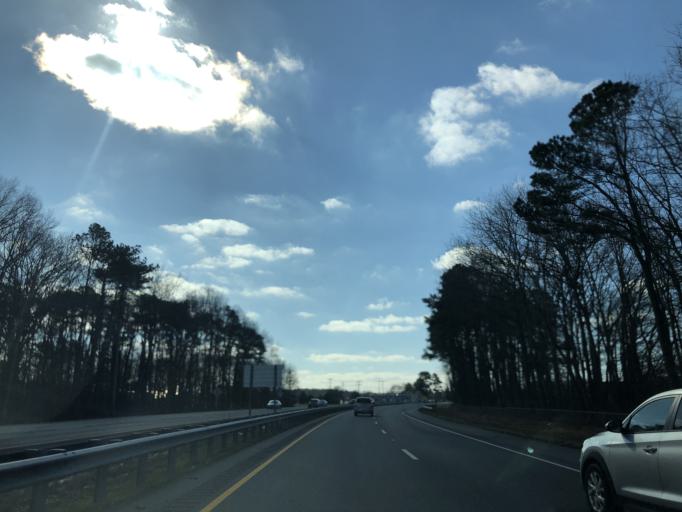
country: US
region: Maryland
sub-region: Worcester County
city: Berlin
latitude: 38.3327
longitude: -75.2101
